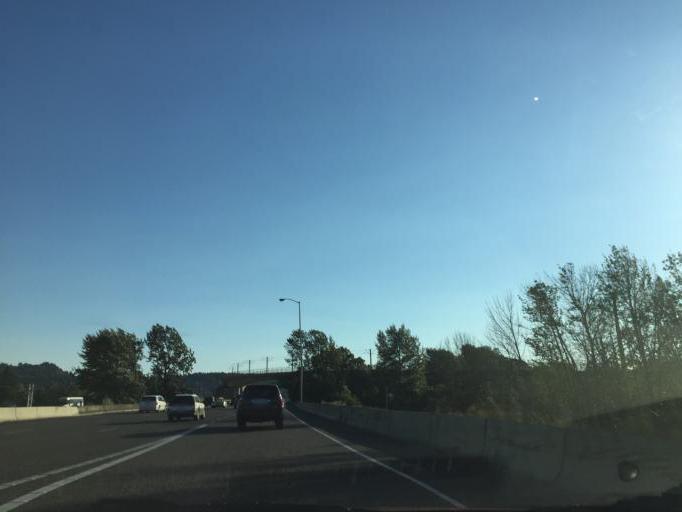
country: US
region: Oregon
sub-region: Multnomah County
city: Lents
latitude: 45.5678
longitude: -122.5545
